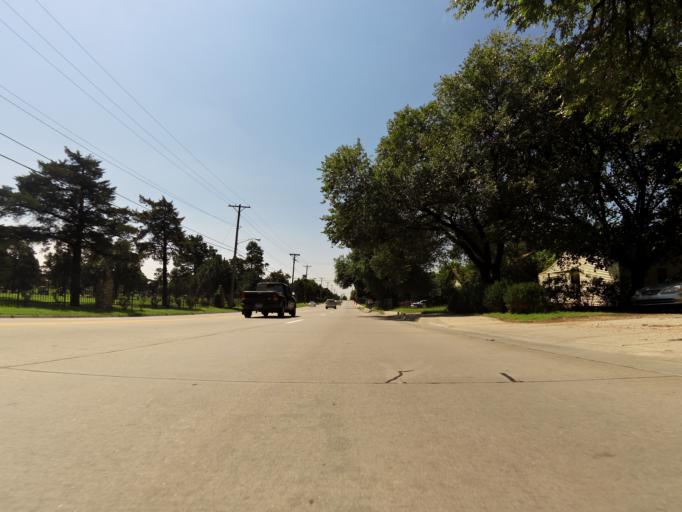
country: US
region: Kansas
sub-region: Sedgwick County
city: Wichita
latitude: 37.7056
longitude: -97.2990
